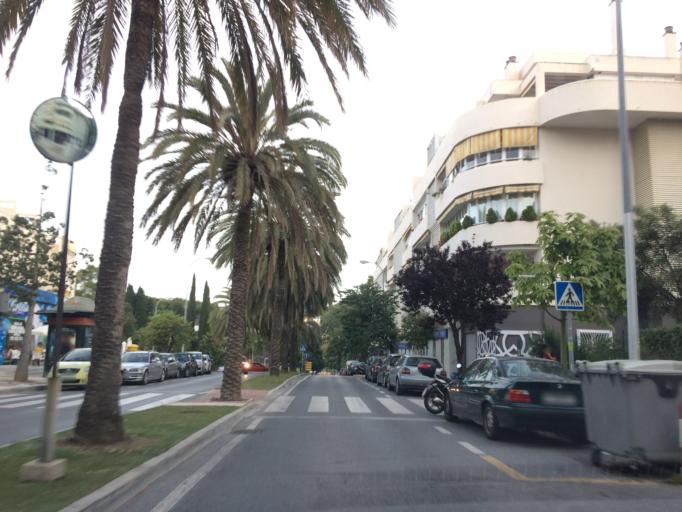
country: ES
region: Andalusia
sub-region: Provincia de Malaga
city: Malaga
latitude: 36.7303
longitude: -4.4029
